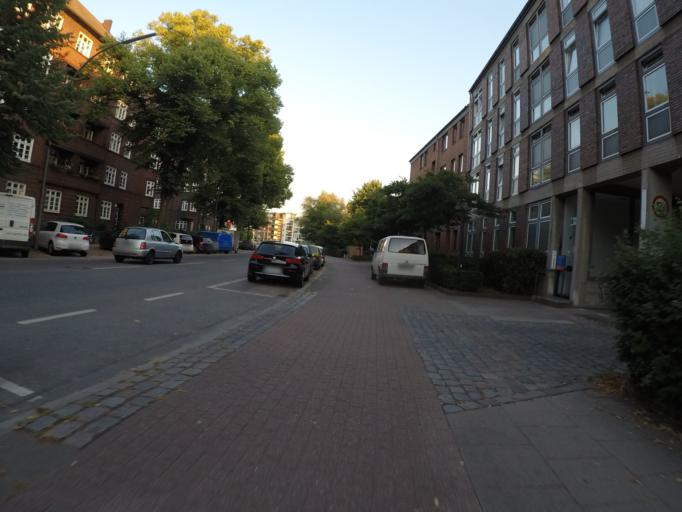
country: DE
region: Hamburg
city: Barmbek-Nord
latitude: 53.5865
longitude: 10.0414
